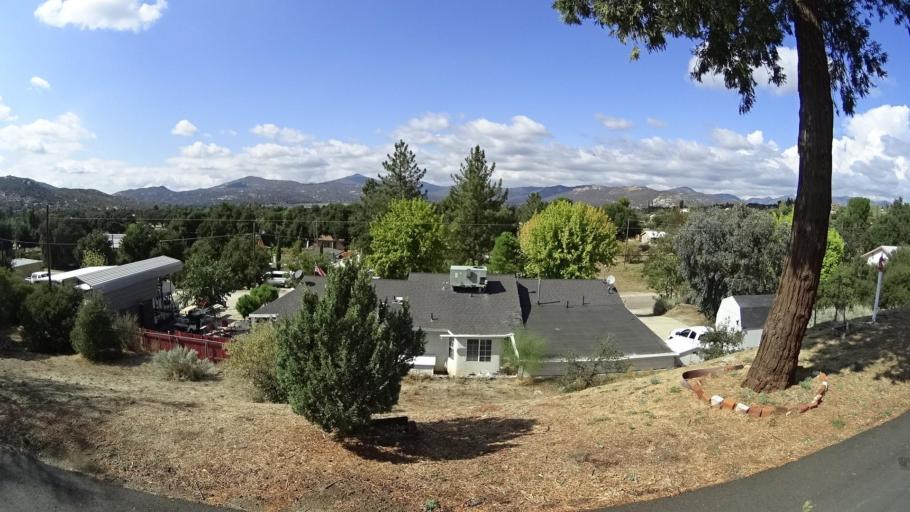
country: US
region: California
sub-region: San Diego County
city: Campo
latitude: 32.6800
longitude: -116.5030
